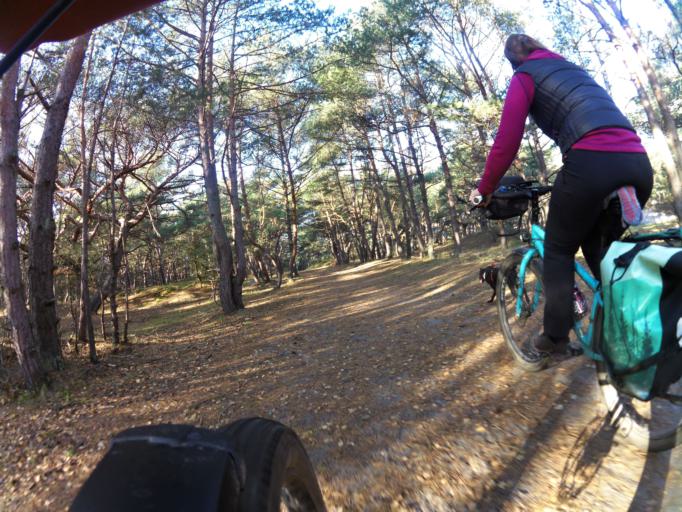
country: PL
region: Pomeranian Voivodeship
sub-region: Powiat pucki
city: Hel
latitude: 54.6045
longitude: 18.8227
